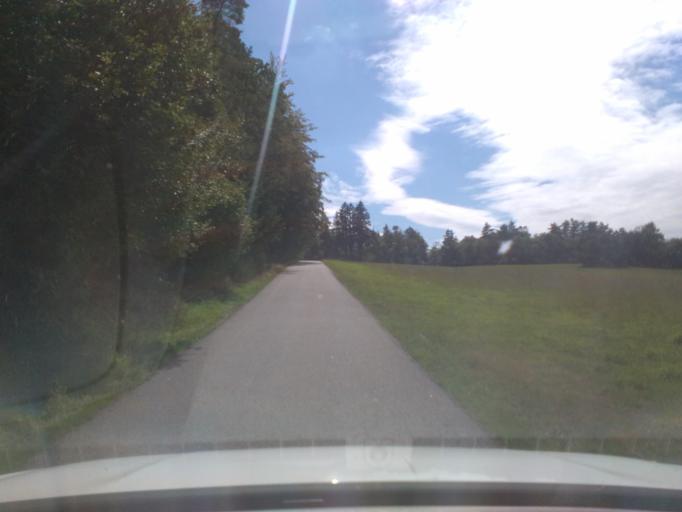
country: FR
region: Lorraine
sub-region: Departement des Vosges
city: Senones
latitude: 48.3600
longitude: 6.9730
